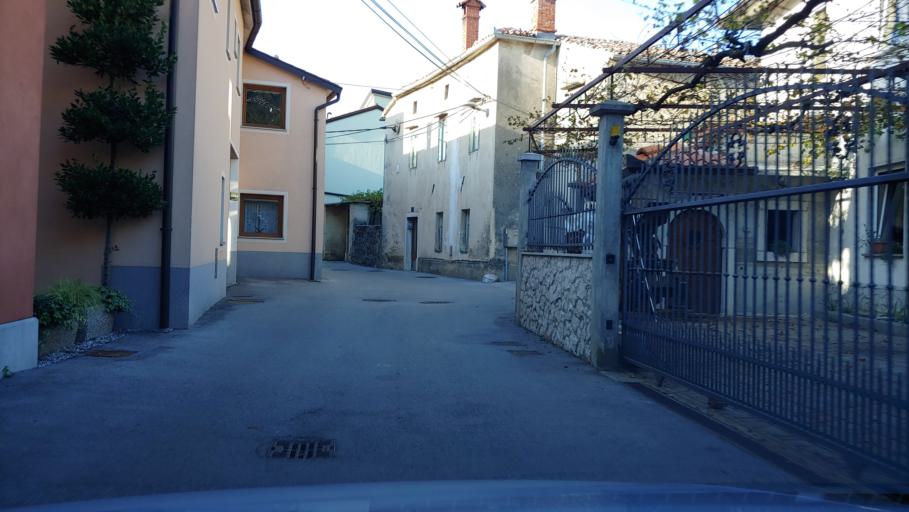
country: SI
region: Vipava
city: Vipava
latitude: 45.8481
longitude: 13.9612
